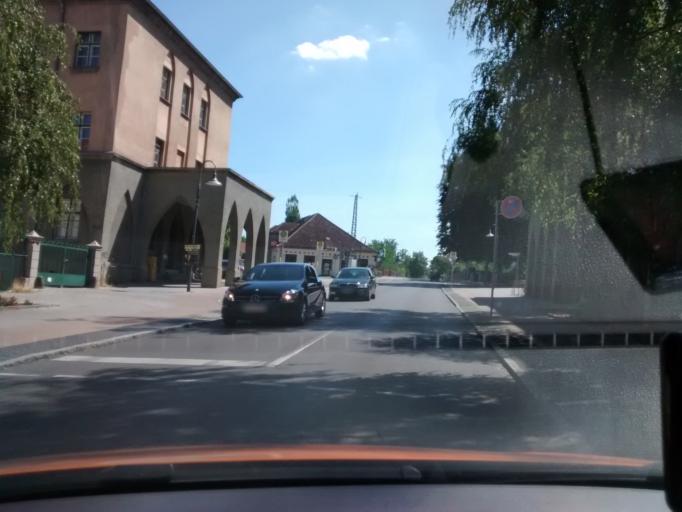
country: DE
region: Brandenburg
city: Birkenwerder
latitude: 52.6879
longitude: 13.2871
